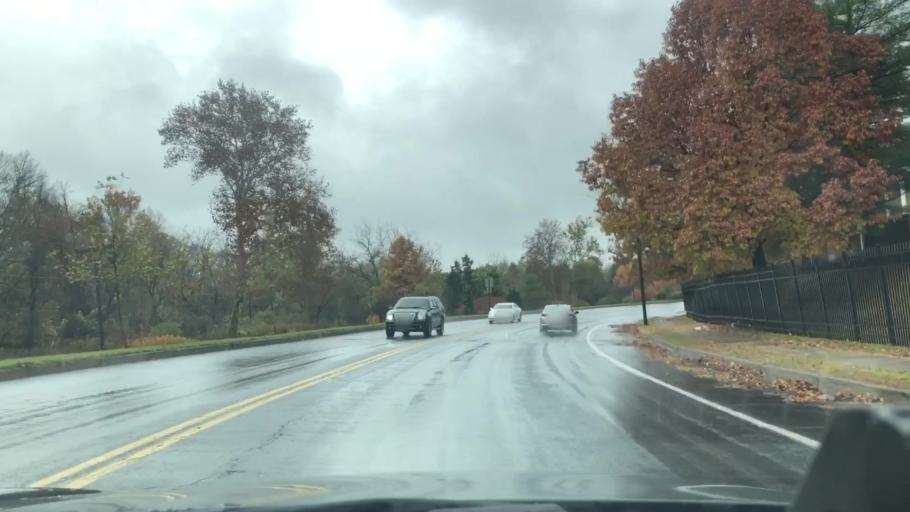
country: US
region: Pennsylvania
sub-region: Lehigh County
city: Allentown
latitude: 40.5992
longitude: -75.4634
